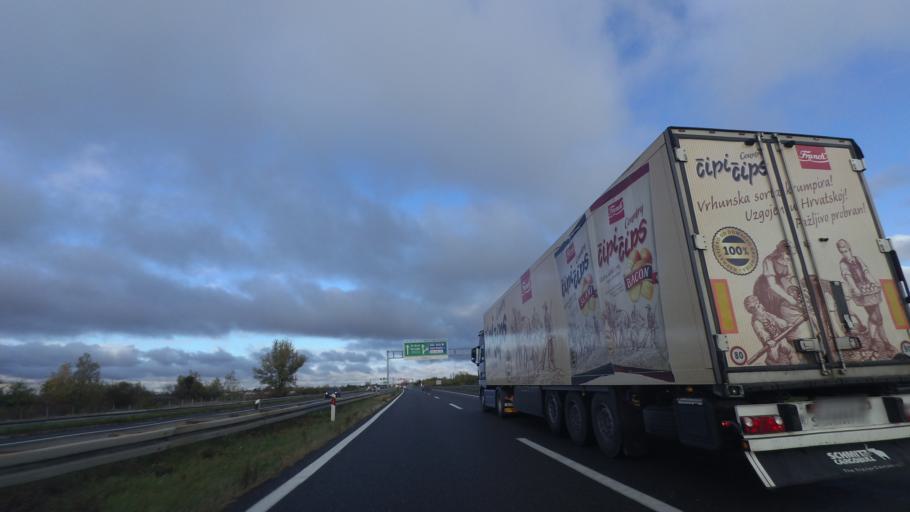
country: HR
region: Zagrebacka
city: Micevec
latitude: 45.7523
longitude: 16.0735
